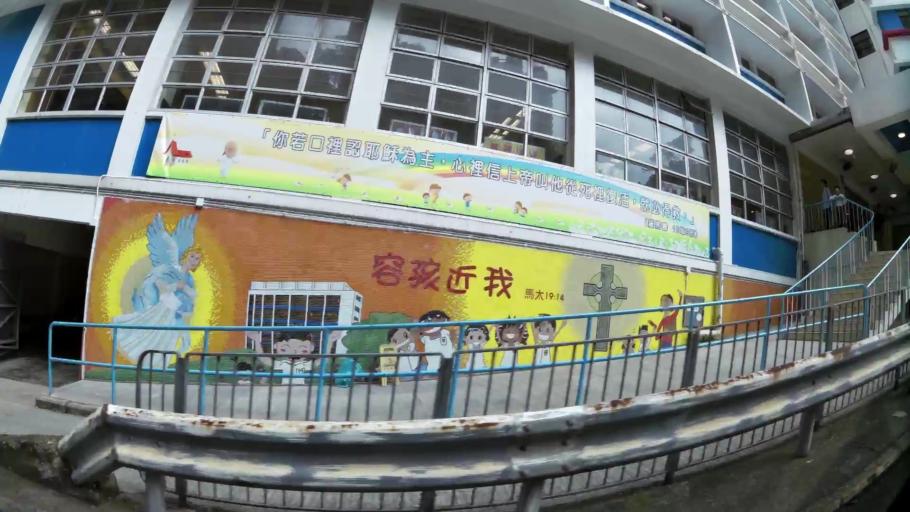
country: HK
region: Wanchai
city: Wan Chai
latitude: 22.2880
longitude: 114.1955
